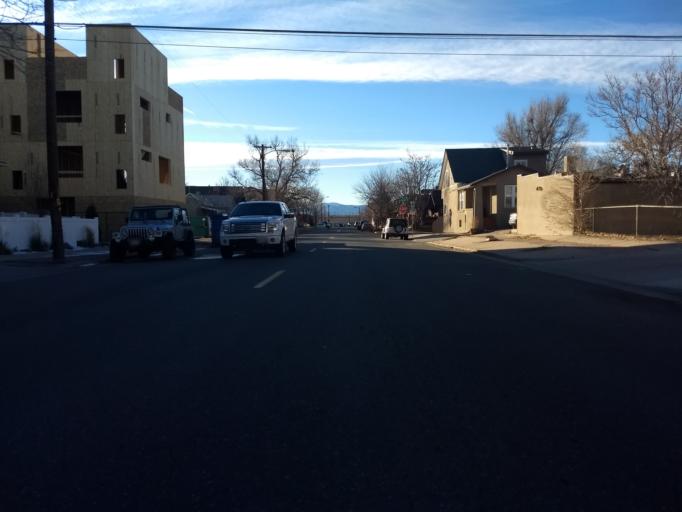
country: US
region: Colorado
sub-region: Denver County
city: Denver
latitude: 39.7184
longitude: -104.9957
